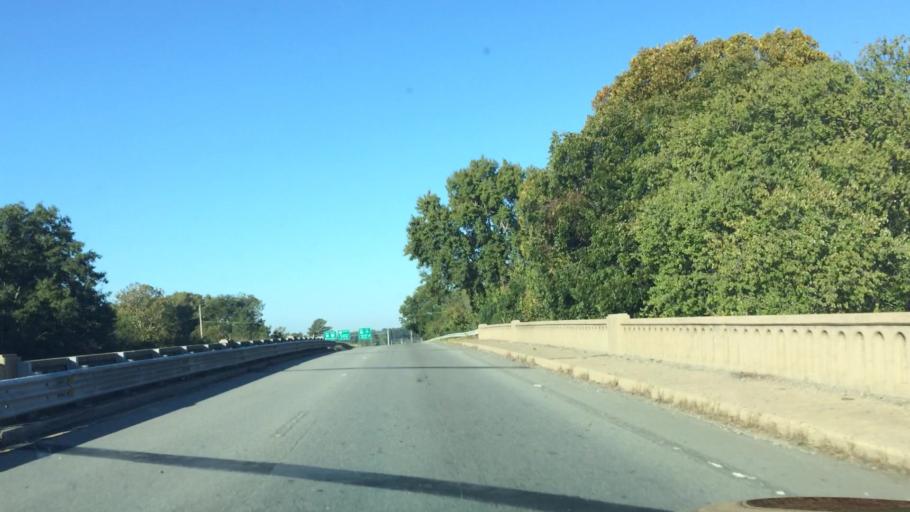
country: US
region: North Carolina
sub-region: Wayne County
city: Goldsboro
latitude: 35.3990
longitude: -77.9959
